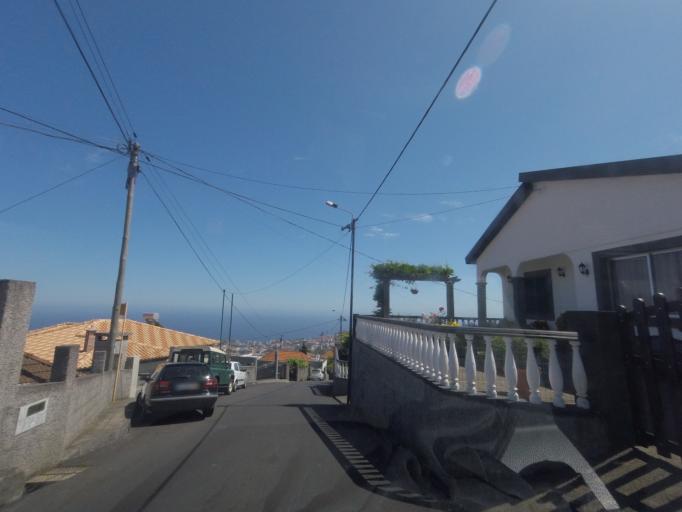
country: PT
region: Madeira
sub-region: Funchal
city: Nossa Senhora do Monte
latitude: 32.6731
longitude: -16.9327
